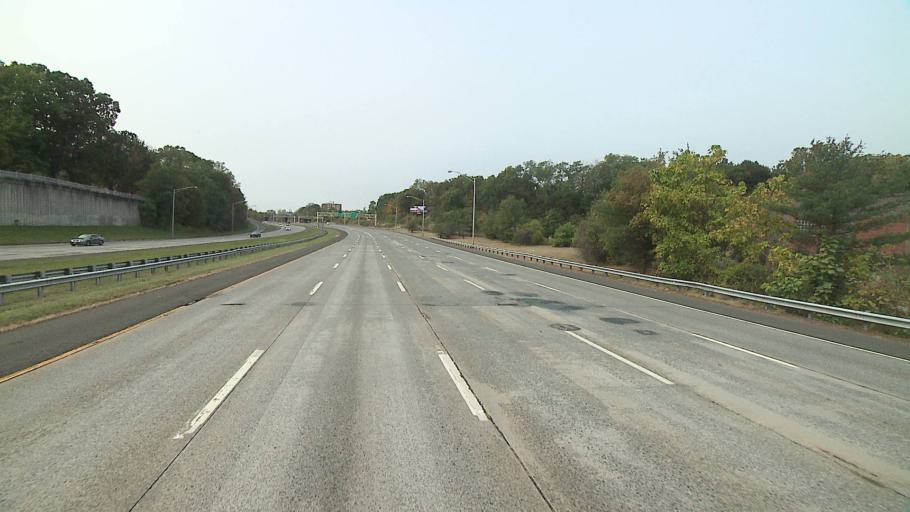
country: US
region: Connecticut
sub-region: Hartford County
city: New Britain
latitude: 41.6779
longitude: -72.7676
